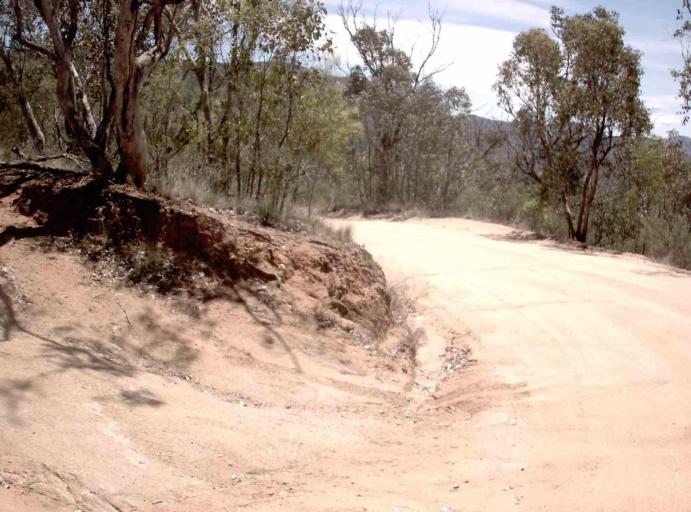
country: AU
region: New South Wales
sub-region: Snowy River
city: Jindabyne
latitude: -36.9356
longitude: 148.3646
